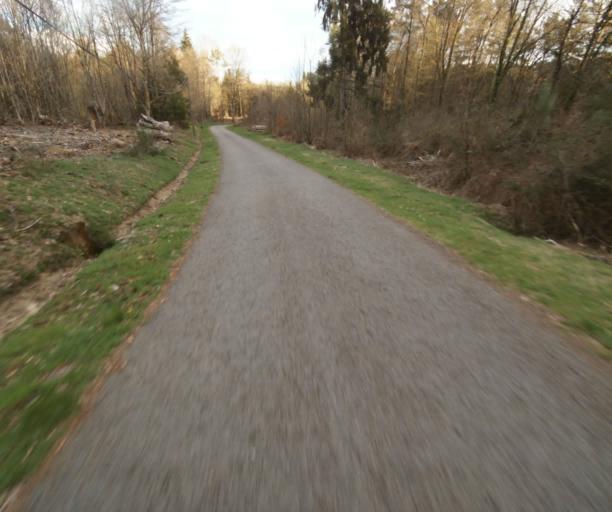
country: FR
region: Limousin
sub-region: Departement de la Correze
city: Argentat
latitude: 45.2304
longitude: 1.9672
